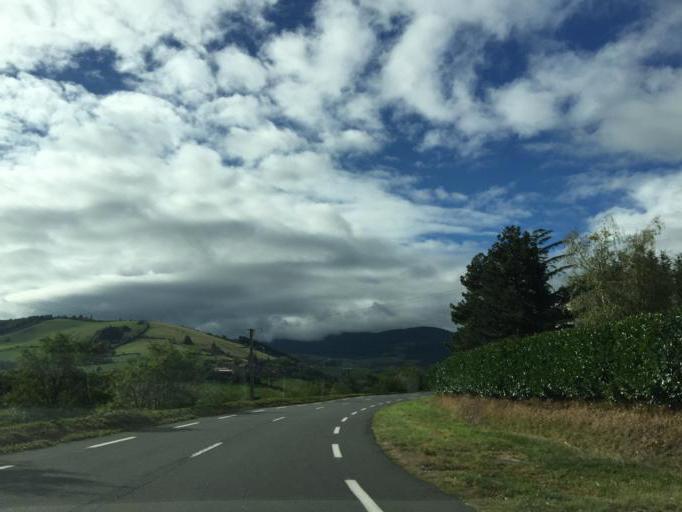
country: FR
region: Rhone-Alpes
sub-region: Departement de la Loire
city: Saint-Paul-en-Jarez
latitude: 45.4645
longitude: 4.5844
